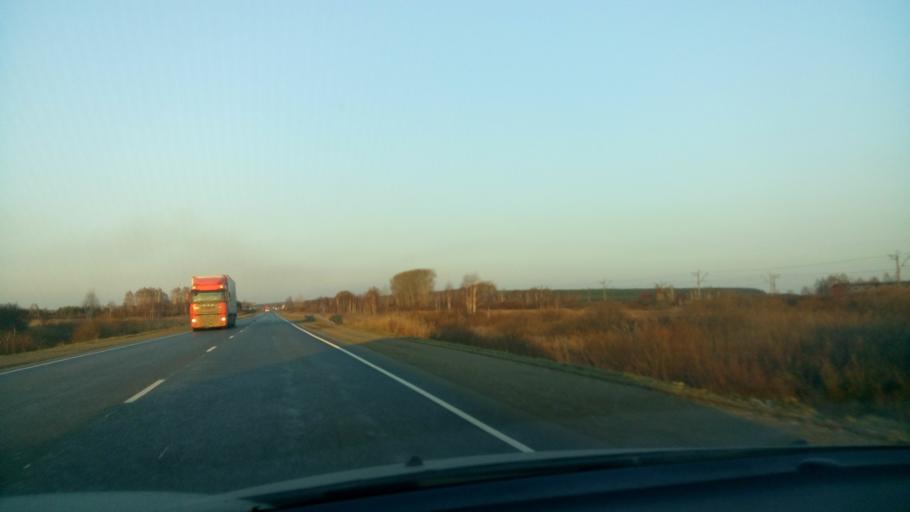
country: RU
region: Sverdlovsk
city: Obukhovskoye
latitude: 56.8301
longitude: 62.5642
